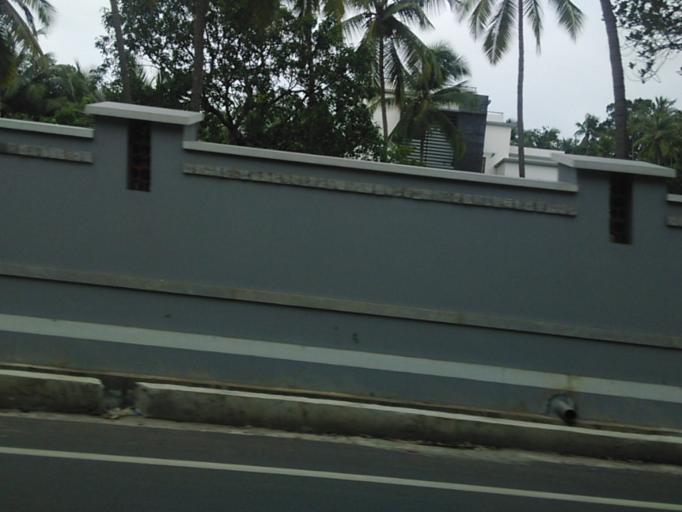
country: IN
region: Kerala
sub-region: Kozhikode
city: Kunnamangalam
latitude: 11.2946
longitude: 75.8390
